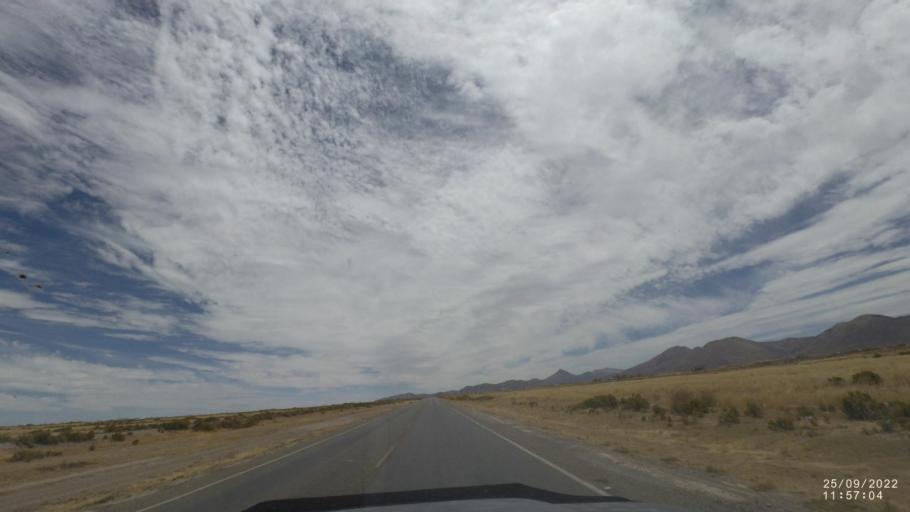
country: BO
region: Oruro
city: Challapata
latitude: -18.8292
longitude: -66.8243
